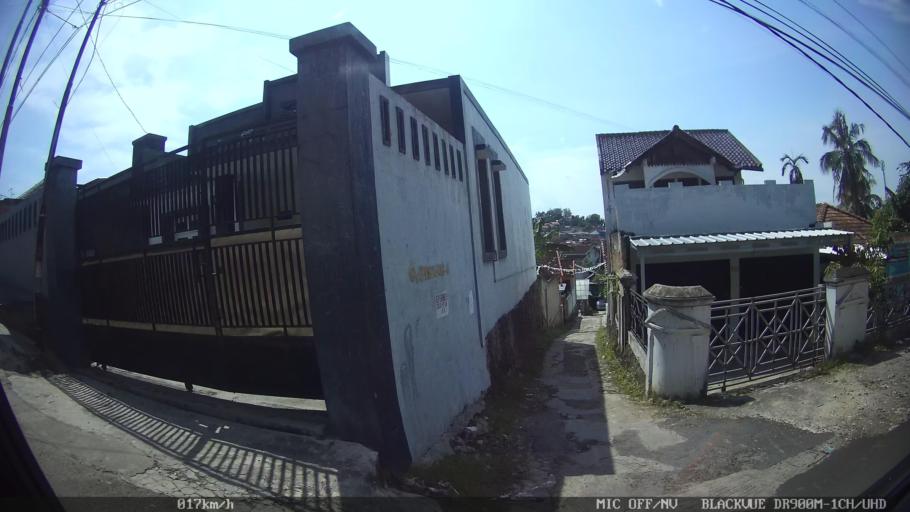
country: ID
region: Lampung
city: Kedaton
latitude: -5.3994
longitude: 105.2509
